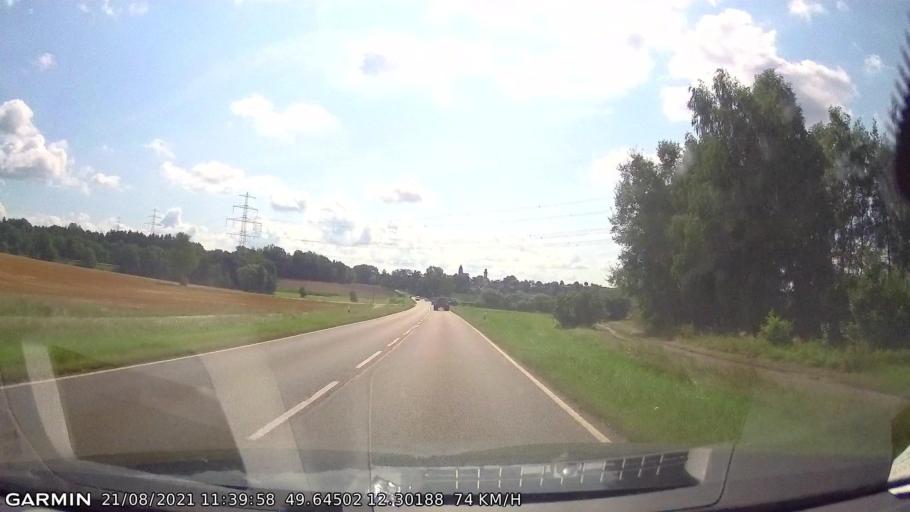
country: DE
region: Bavaria
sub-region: Upper Palatinate
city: Waldthurn
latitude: 49.6451
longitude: 12.3018
